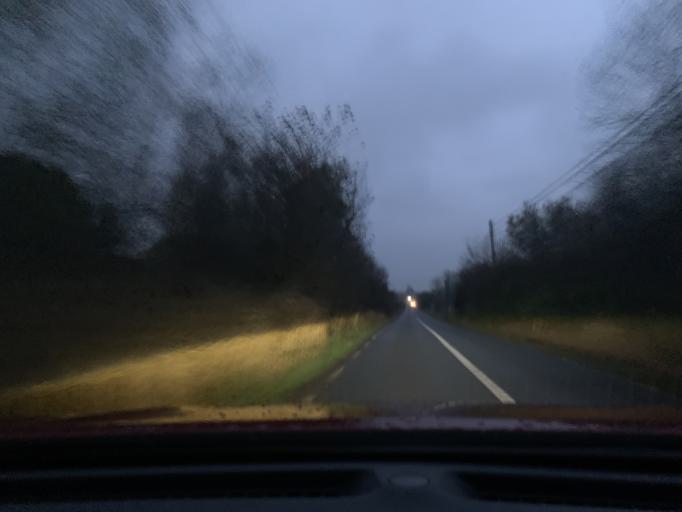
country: IE
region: Connaught
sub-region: Sligo
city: Ballymote
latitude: 54.0740
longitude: -8.5115
